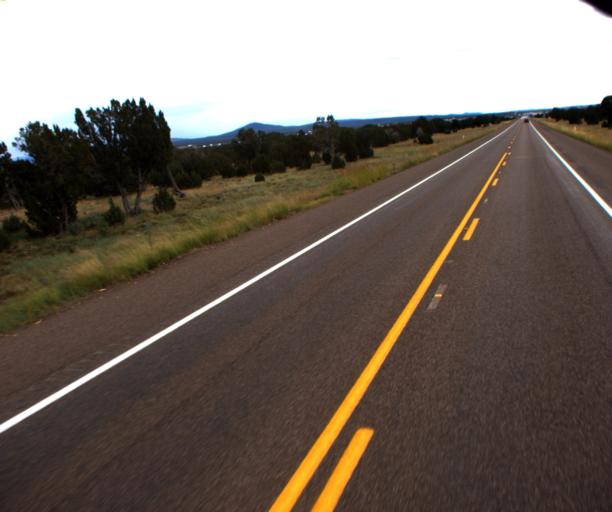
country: US
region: Arizona
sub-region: Navajo County
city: Show Low
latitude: 34.2845
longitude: -110.0288
